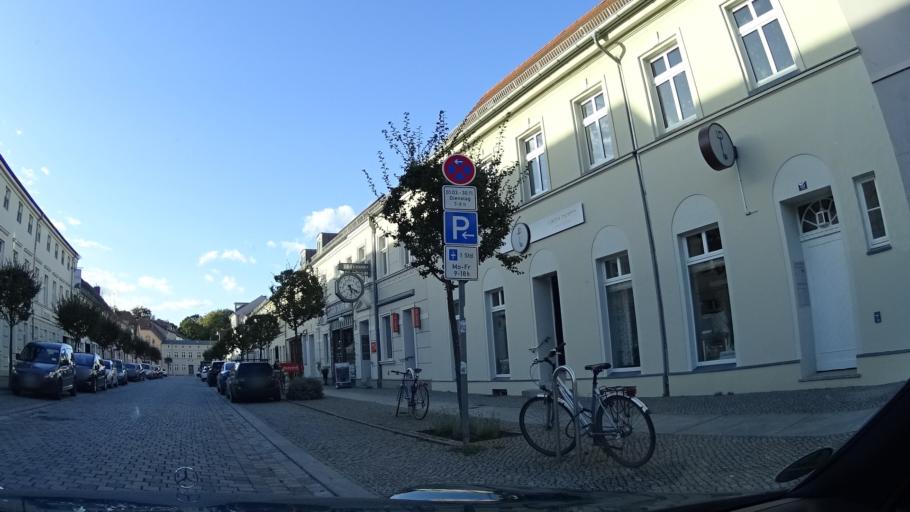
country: DE
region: Brandenburg
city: Neuruppin
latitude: 52.9255
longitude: 12.8057
